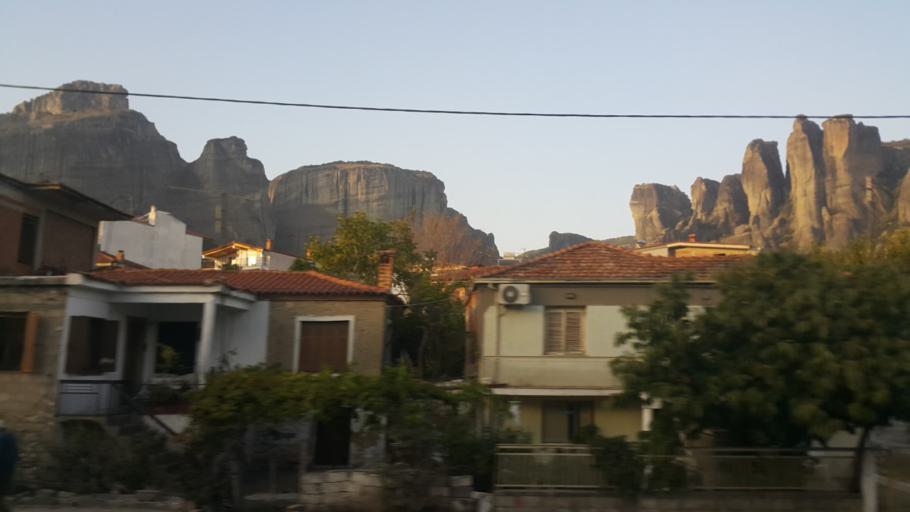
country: GR
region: Thessaly
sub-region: Trikala
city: Kalampaka
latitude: 39.7021
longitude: 21.6294
